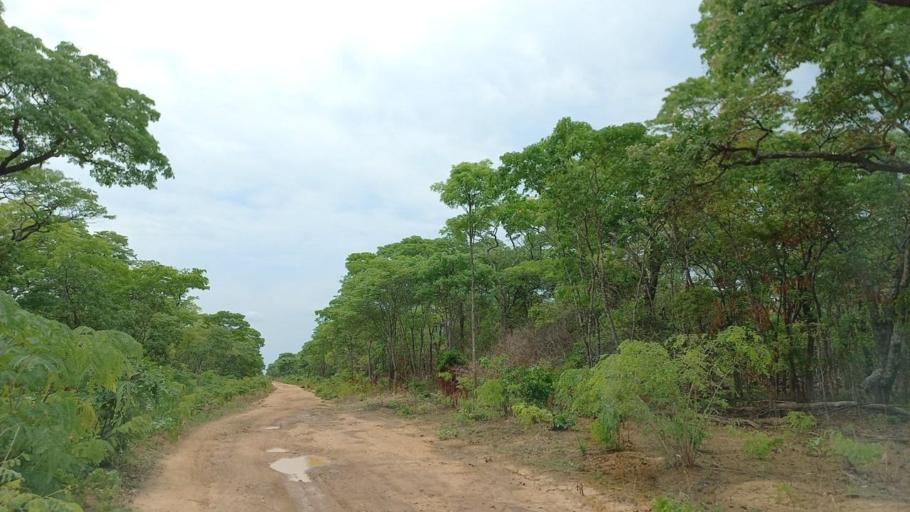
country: ZM
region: North-Western
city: Kalengwa
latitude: -13.5895
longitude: 24.9724
